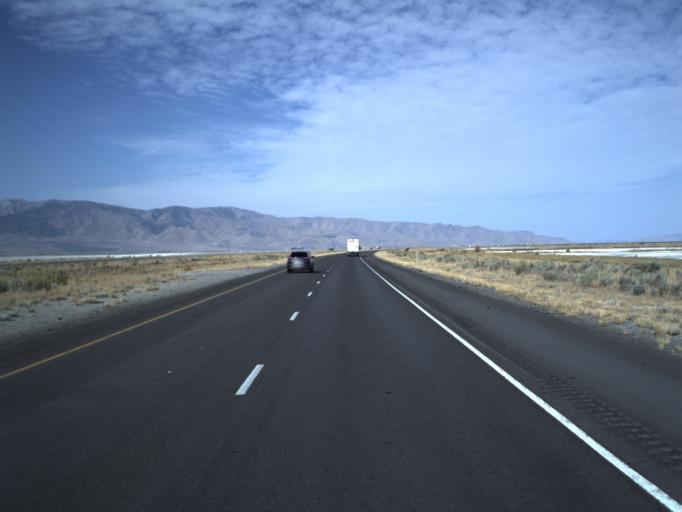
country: US
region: Utah
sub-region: Tooele County
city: Stansbury park
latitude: 40.6627
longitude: -112.3459
